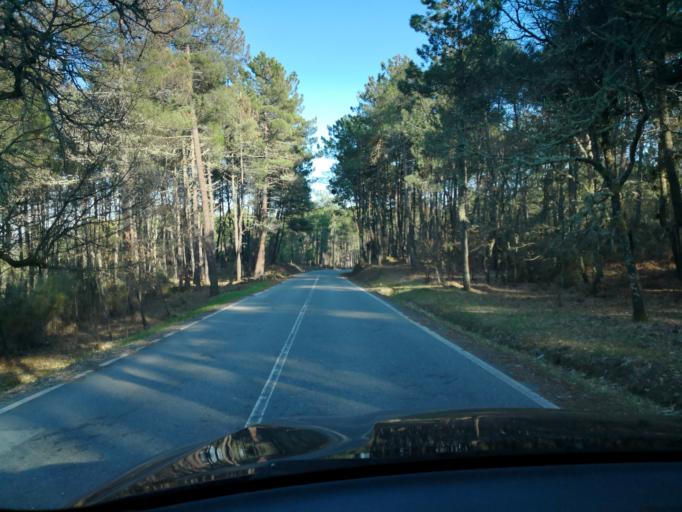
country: PT
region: Vila Real
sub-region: Sabrosa
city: Sabrosa
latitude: 41.3526
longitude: -7.6079
